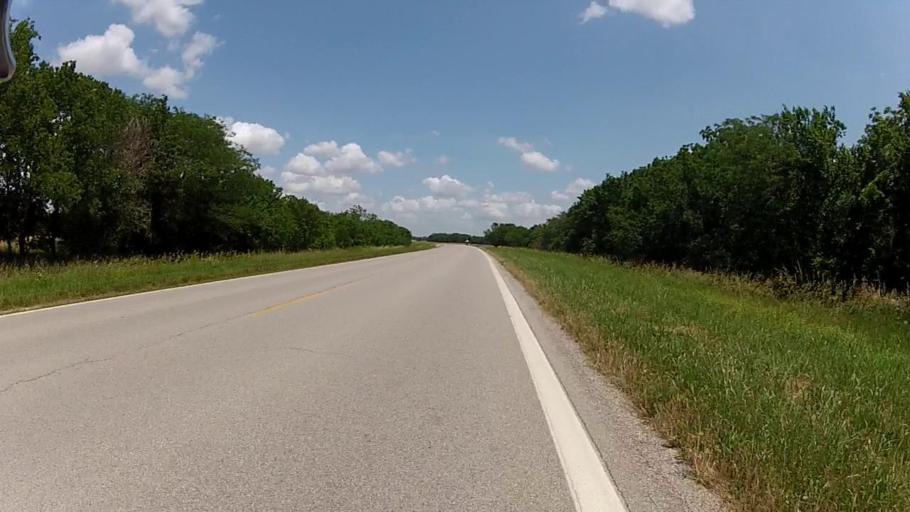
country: US
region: Kansas
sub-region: Labette County
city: Altamont
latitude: 37.1930
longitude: -95.3881
